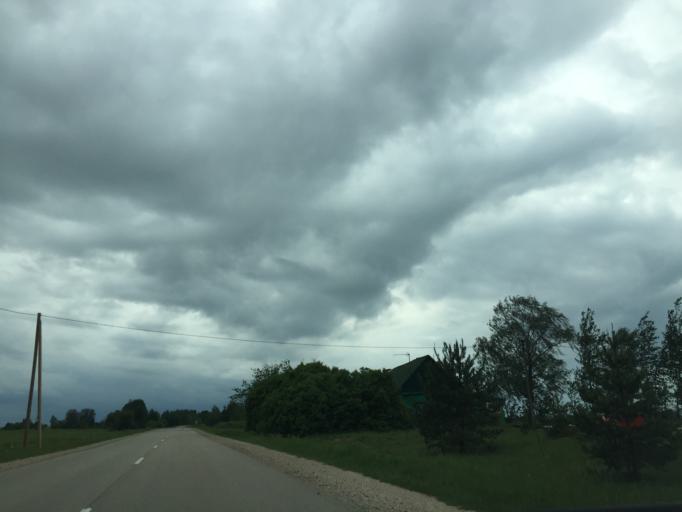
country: LV
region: Preilu Rajons
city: Preili
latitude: 56.0759
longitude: 26.7173
